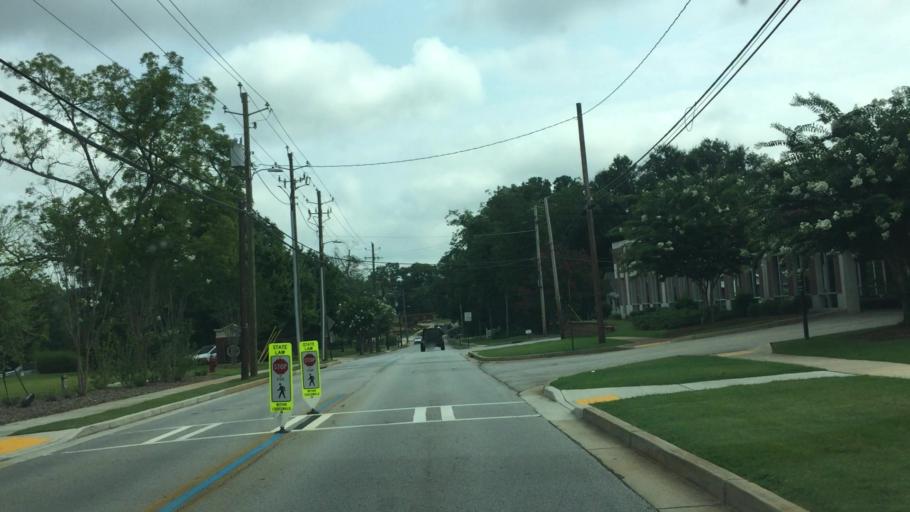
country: US
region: Georgia
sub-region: Henry County
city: McDonough
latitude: 33.4494
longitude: -84.1455
